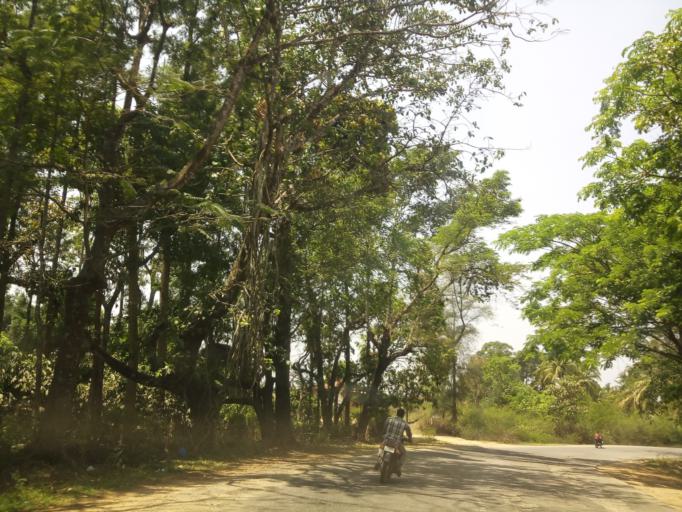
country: IN
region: Karnataka
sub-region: Hassan
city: Sakleshpur
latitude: 12.9539
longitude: 75.8594
